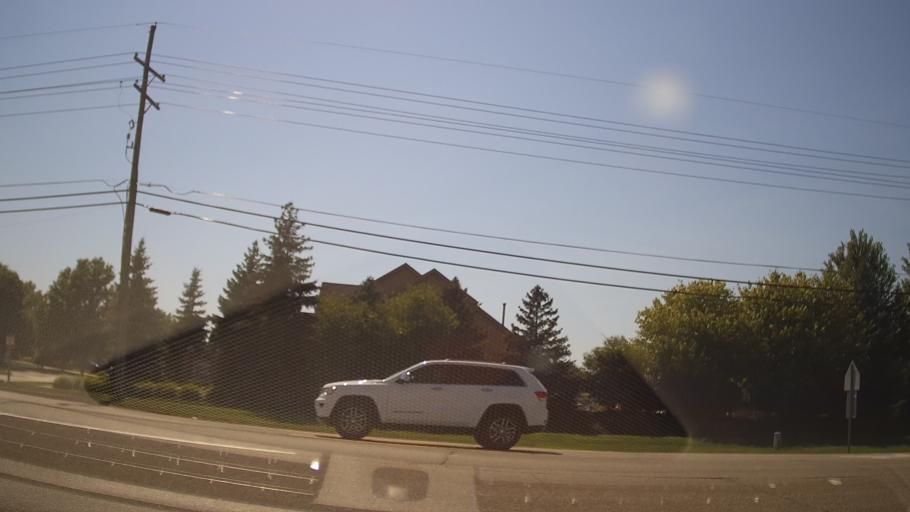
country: US
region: Michigan
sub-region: Macomb County
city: Clinton
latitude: 42.6512
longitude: -82.9167
